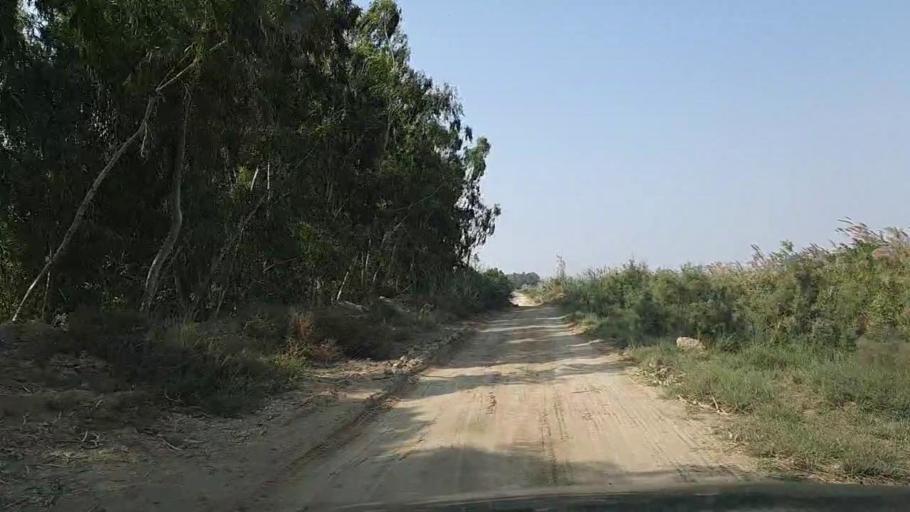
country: PK
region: Sindh
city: Gharo
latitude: 24.7220
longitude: 67.6794
